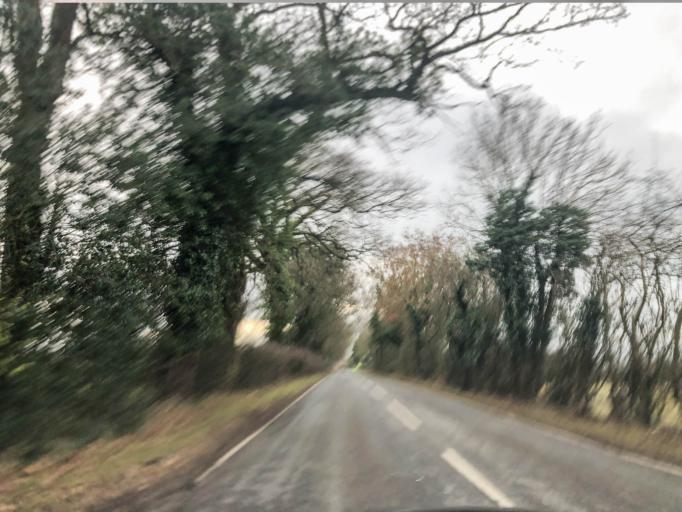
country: GB
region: England
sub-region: Warwickshire
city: Wroxall
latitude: 52.3236
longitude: -1.6695
